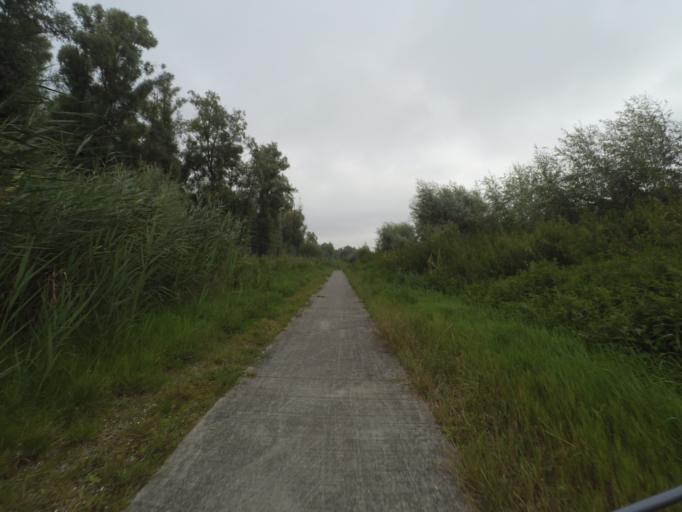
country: NL
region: Flevoland
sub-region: Gemeente Lelystad
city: Lelystad
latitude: 52.4426
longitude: 5.4251
